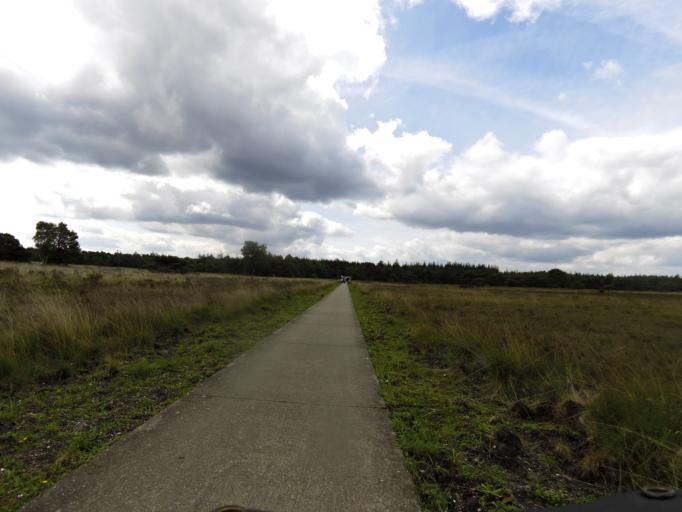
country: NL
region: Gelderland
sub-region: Gemeente Apeldoorn
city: Uddel
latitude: 52.3074
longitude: 5.8089
